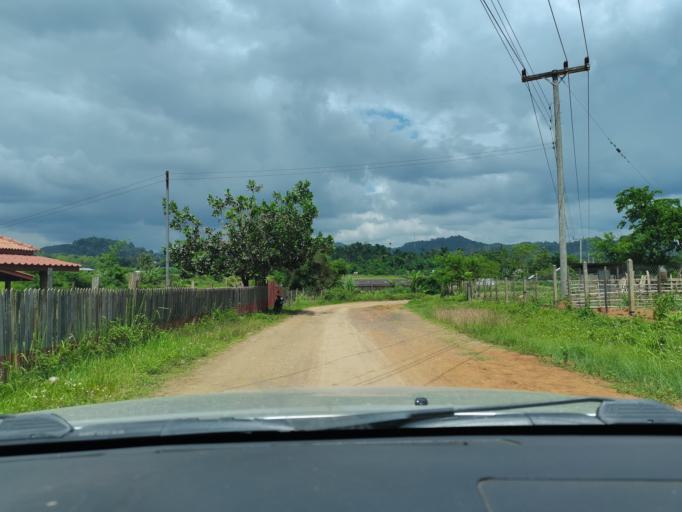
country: LA
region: Loungnamtha
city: Muang Long
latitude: 20.6829
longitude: 101.0499
